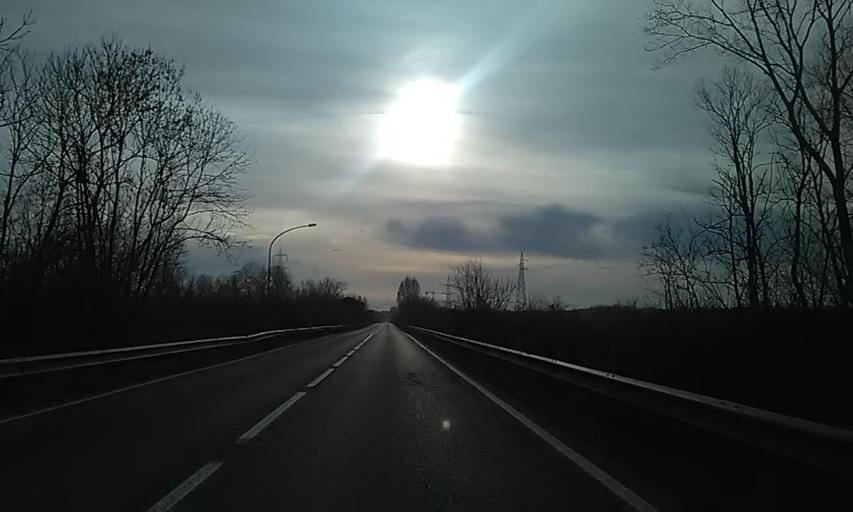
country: IT
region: Piedmont
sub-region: Provincia di Torino
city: Rondissone
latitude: 45.2658
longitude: 7.9767
